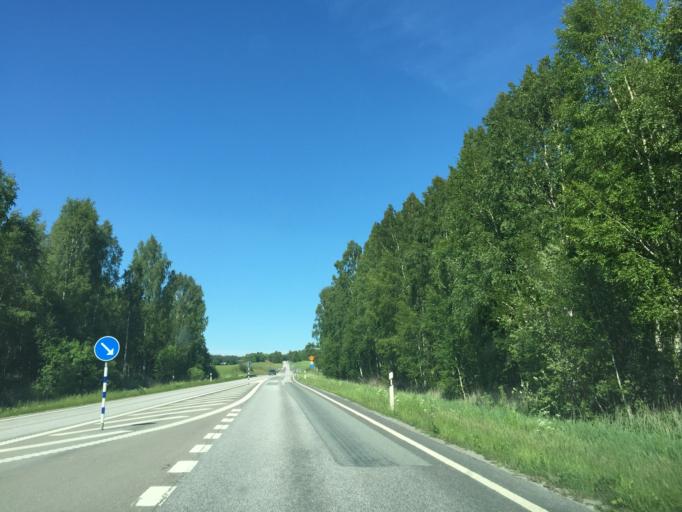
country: SE
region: OEstergoetland
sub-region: Motala Kommun
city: Ryd
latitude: 58.6830
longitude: 14.9636
